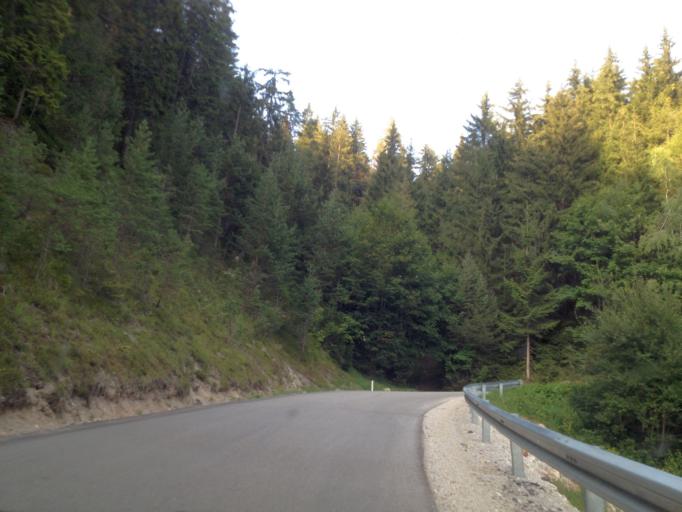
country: AT
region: Styria
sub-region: Politischer Bezirk Liezen
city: Schladming
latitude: 47.4003
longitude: 13.6148
